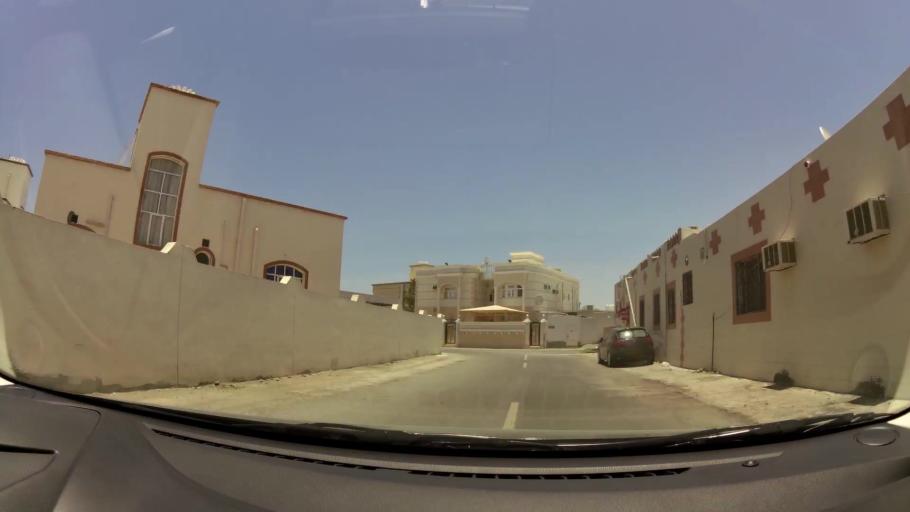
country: OM
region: Muhafazat Masqat
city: As Sib al Jadidah
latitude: 23.6370
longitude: 58.2289
